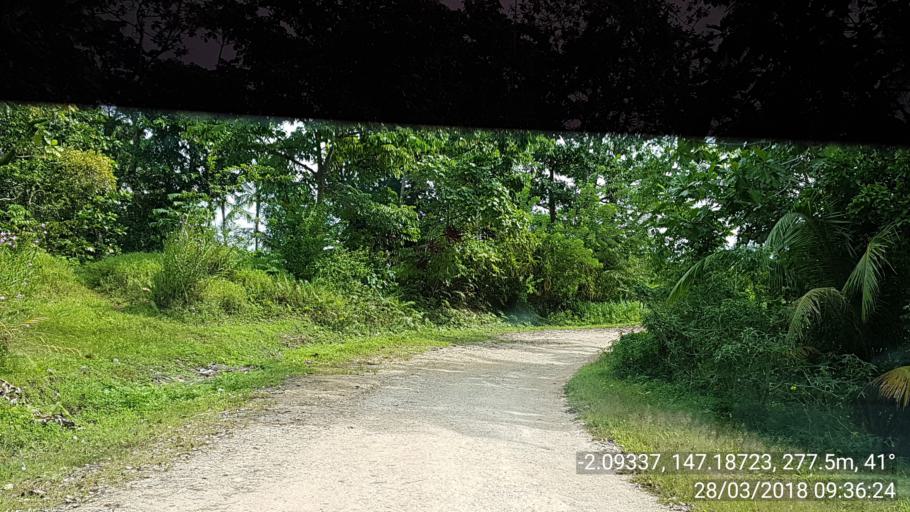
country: PG
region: Manus
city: Lorengau
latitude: -2.0933
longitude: 147.1872
